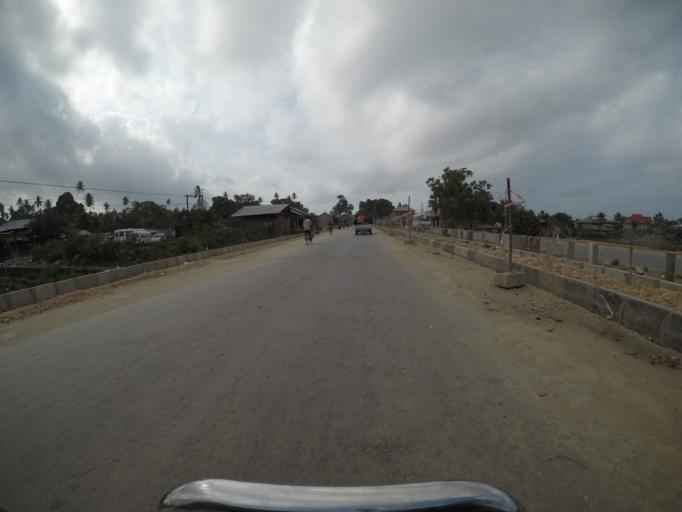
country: TZ
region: Zanzibar Urban/West
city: Zanzibar
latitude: -6.1791
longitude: 39.2285
